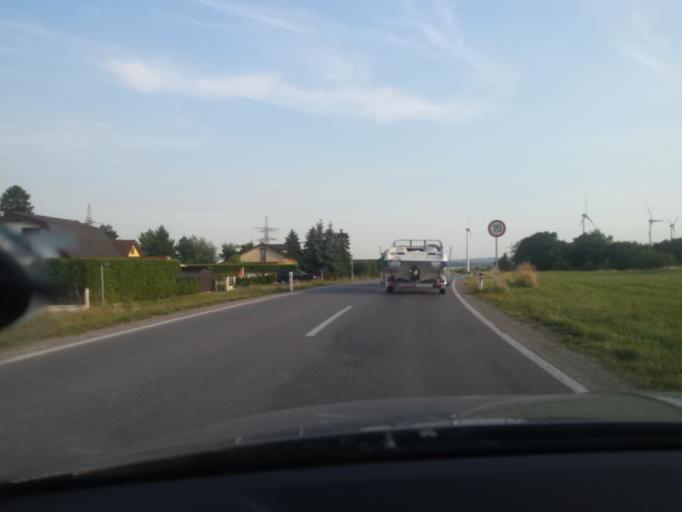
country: AT
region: Lower Austria
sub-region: Politischer Bezirk Bruck an der Leitha
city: Petronell-Carnuntum
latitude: 48.0990
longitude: 16.8635
